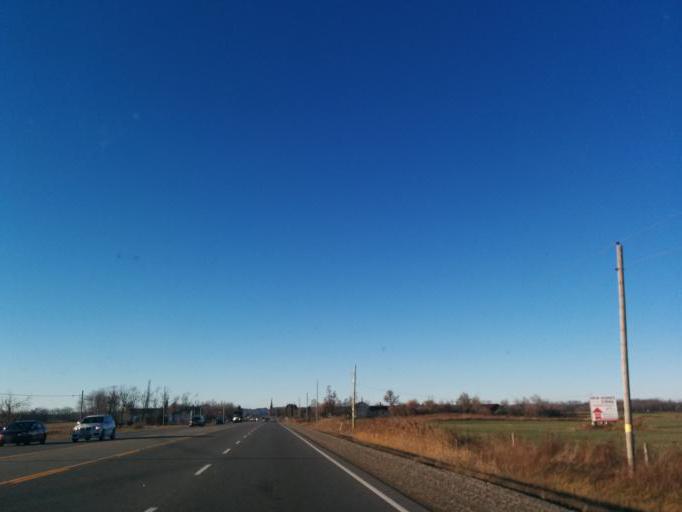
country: CA
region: Ontario
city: Brampton
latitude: 43.7900
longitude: -79.9005
